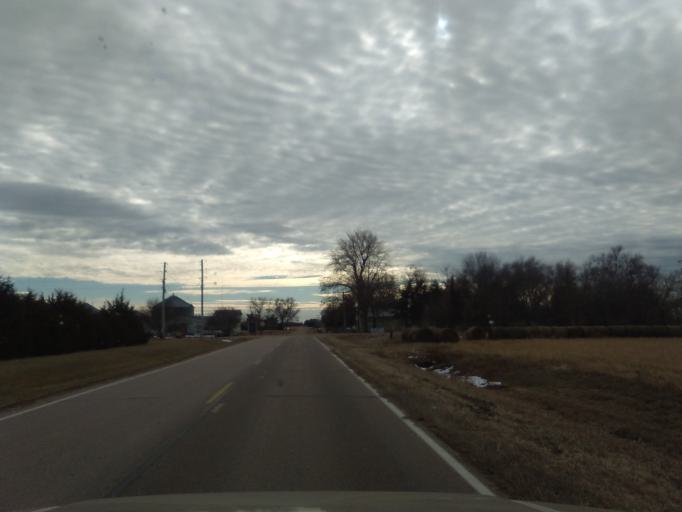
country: US
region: Nebraska
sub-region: Buffalo County
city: Gibbon
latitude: 40.6485
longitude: -98.8473
